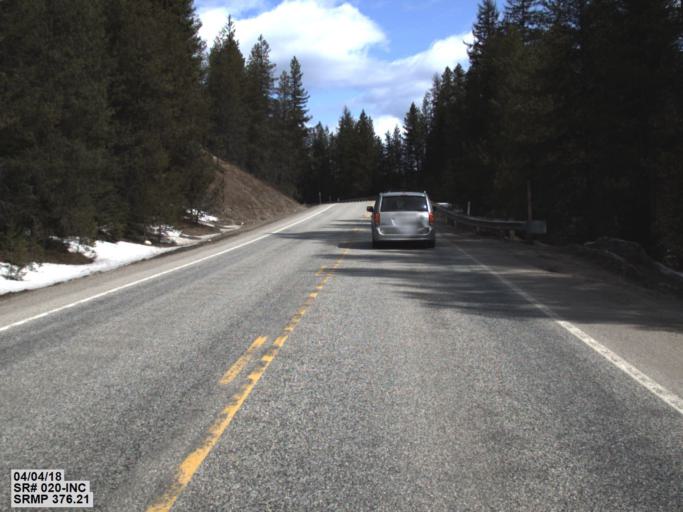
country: US
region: Washington
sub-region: Stevens County
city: Chewelah
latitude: 48.5725
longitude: -117.5536
